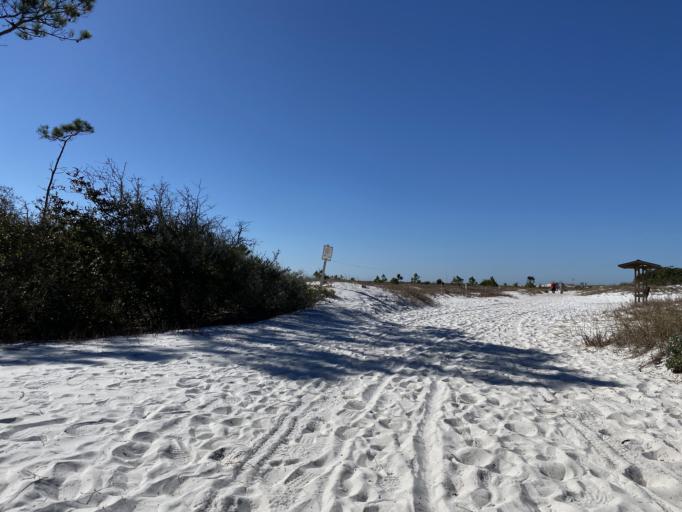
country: US
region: Florida
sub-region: Bay County
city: Laguna Beach
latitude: 30.2707
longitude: -85.9906
